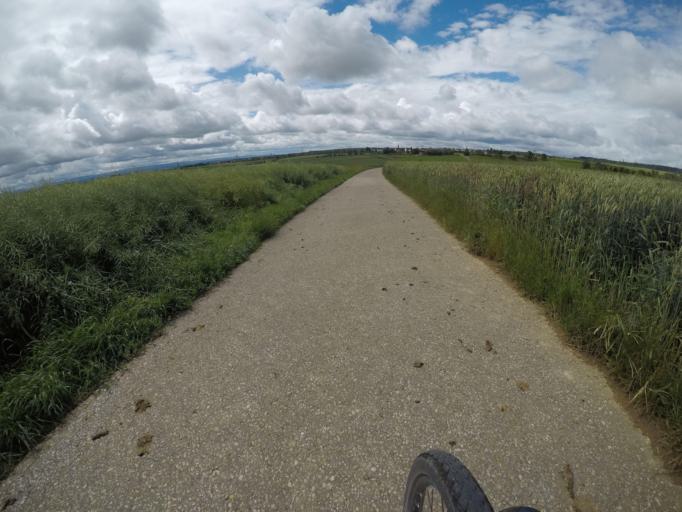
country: DE
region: Baden-Wuerttemberg
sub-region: Regierungsbezirk Stuttgart
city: Deckenpfronn
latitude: 48.6339
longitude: 8.8436
